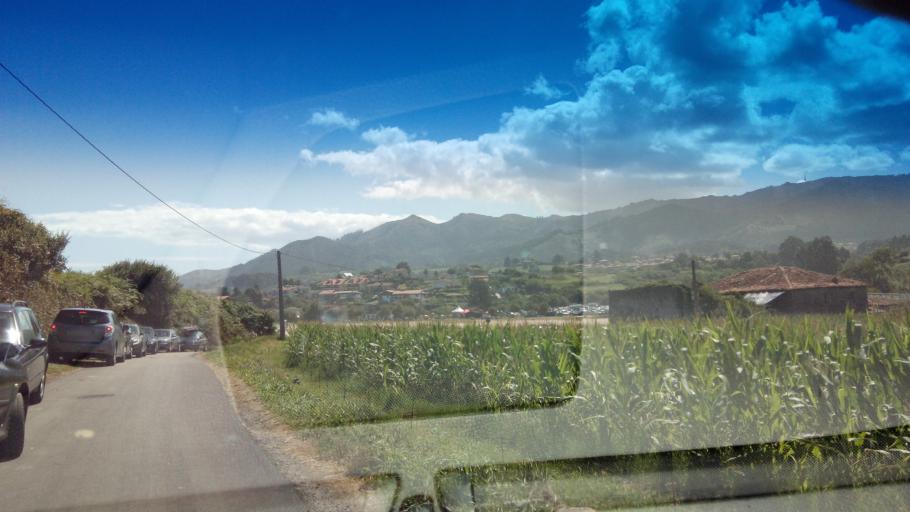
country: ES
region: Asturias
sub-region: Province of Asturias
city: Colunga
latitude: 43.4748
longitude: -5.2177
